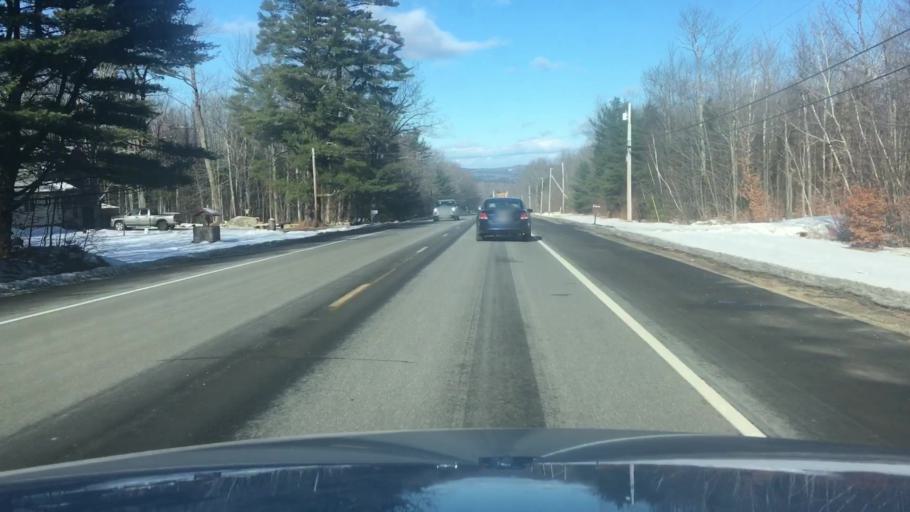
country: US
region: Maine
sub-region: Somerset County
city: Fairfield
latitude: 44.6274
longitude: -69.6760
